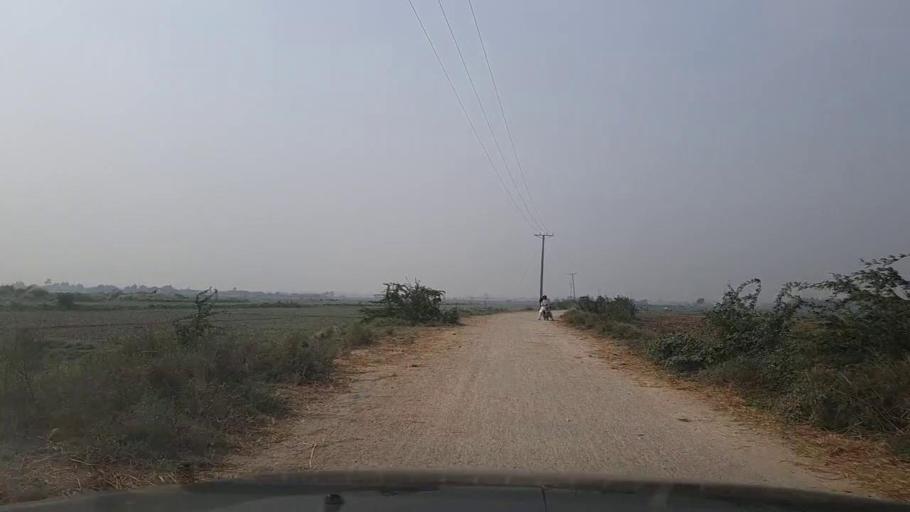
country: PK
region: Sindh
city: Mirpur Sakro
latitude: 24.5470
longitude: 67.8293
